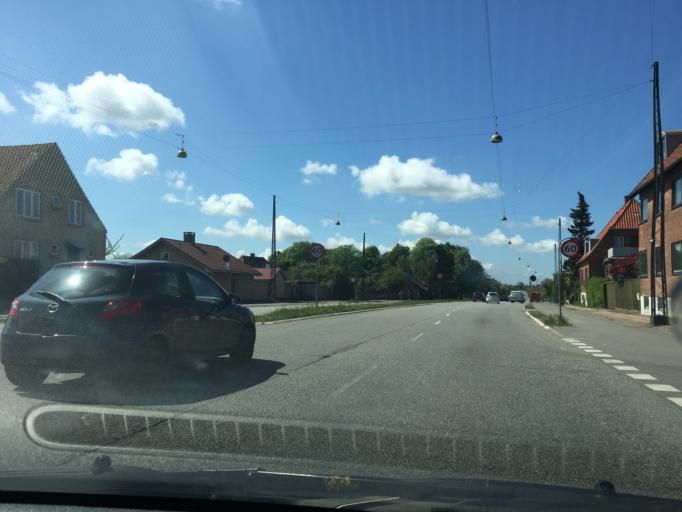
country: DK
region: Capital Region
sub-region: Kobenhavn
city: Vanlose
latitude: 55.6910
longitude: 12.4751
